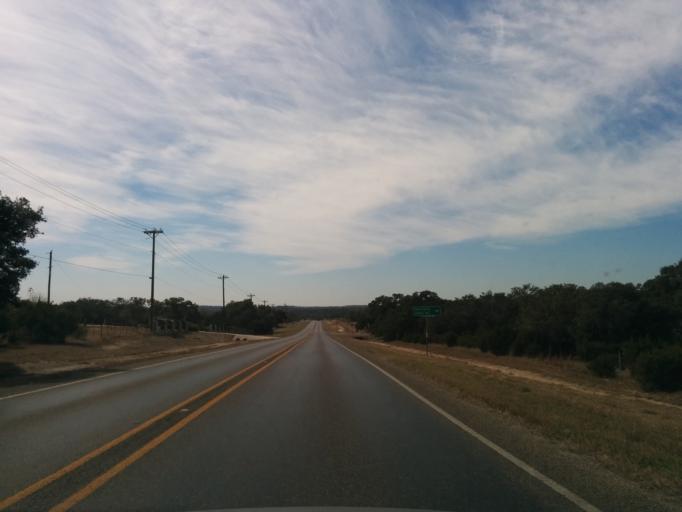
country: US
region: Texas
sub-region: Bexar County
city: Fair Oaks Ranch
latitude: 29.8193
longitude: -98.5806
